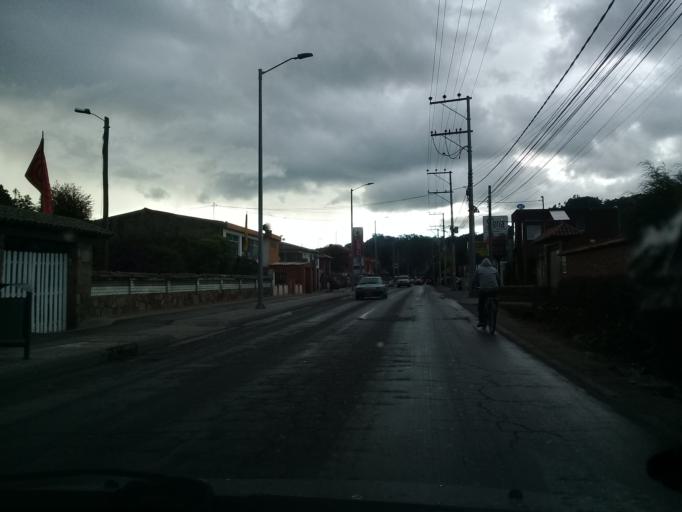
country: CO
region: Cundinamarca
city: Cajica
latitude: 4.9235
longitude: -74.0413
